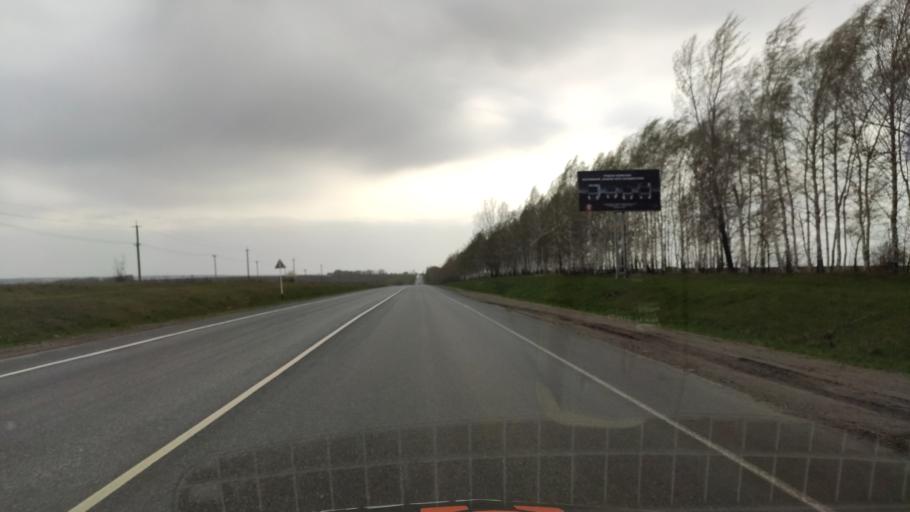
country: RU
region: Kursk
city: Gorshechnoye
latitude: 51.5050
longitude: 37.9920
